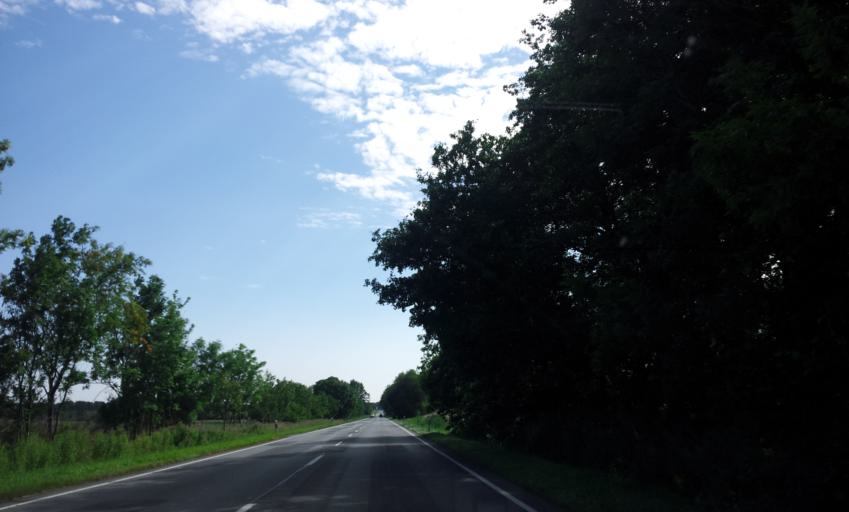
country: DE
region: Mecklenburg-Vorpommern
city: Bergen auf Ruegen
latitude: 54.4154
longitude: 13.4020
